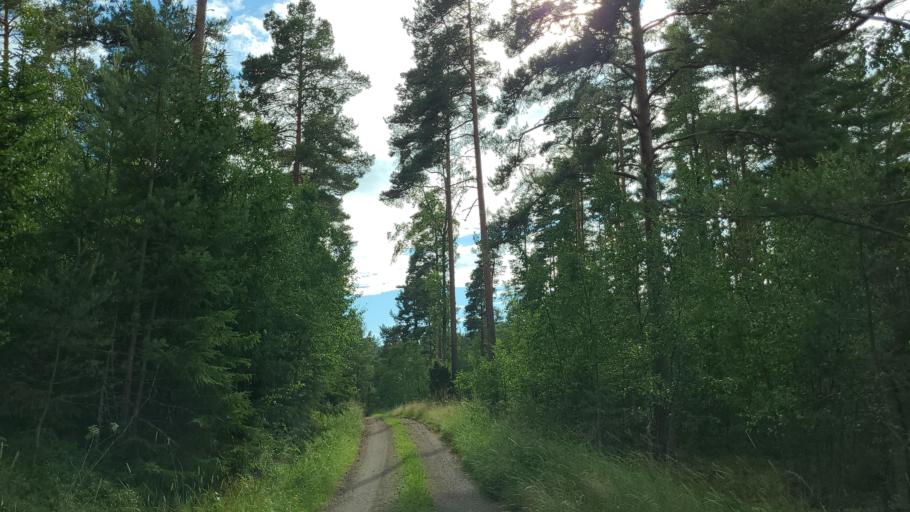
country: FI
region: Varsinais-Suomi
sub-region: Aboland-Turunmaa
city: Nagu
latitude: 60.2855
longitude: 21.9072
